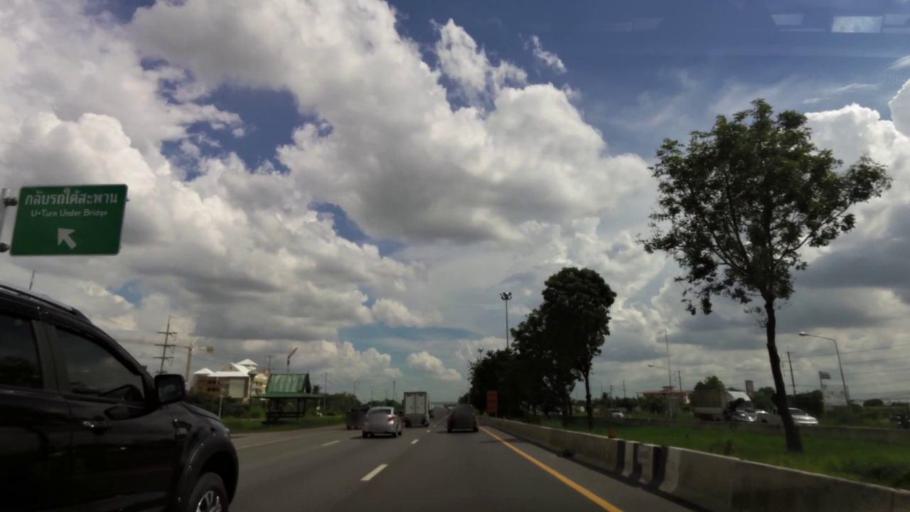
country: TH
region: Phra Nakhon Si Ayutthaya
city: Phra Nakhon Si Ayutthaya
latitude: 14.3991
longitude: 100.5909
